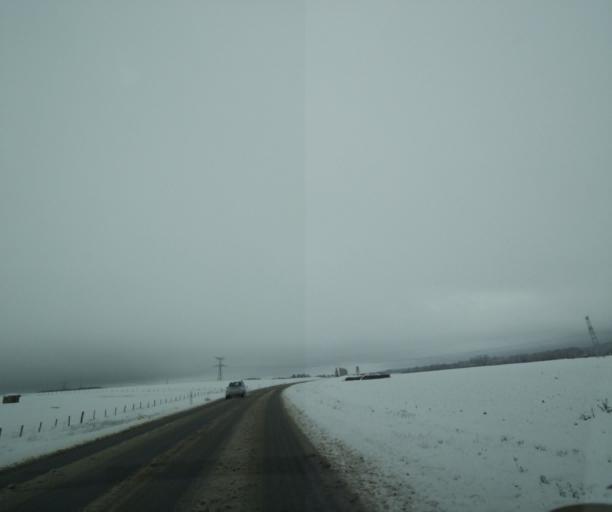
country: FR
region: Champagne-Ardenne
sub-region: Departement de la Haute-Marne
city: Wassy
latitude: 48.5227
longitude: 4.9320
